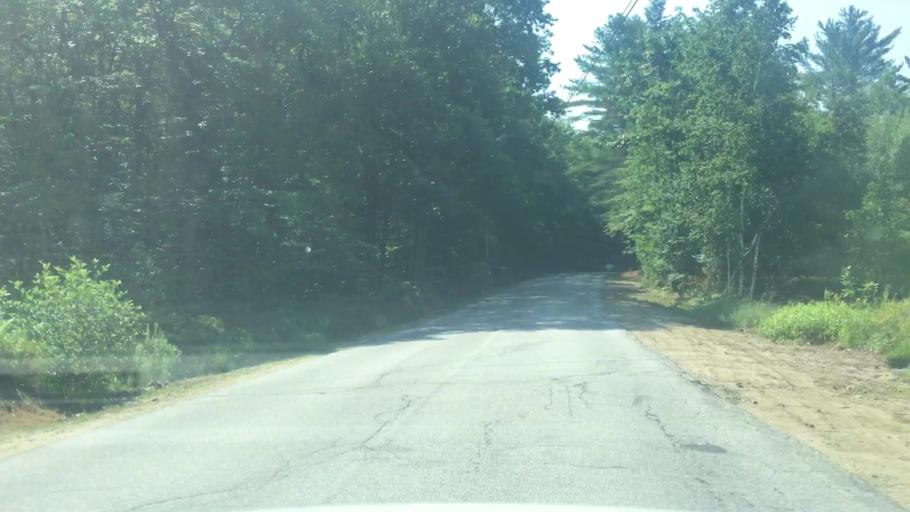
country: US
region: Maine
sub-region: Oxford County
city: South Paris
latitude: 44.2092
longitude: -70.5132
